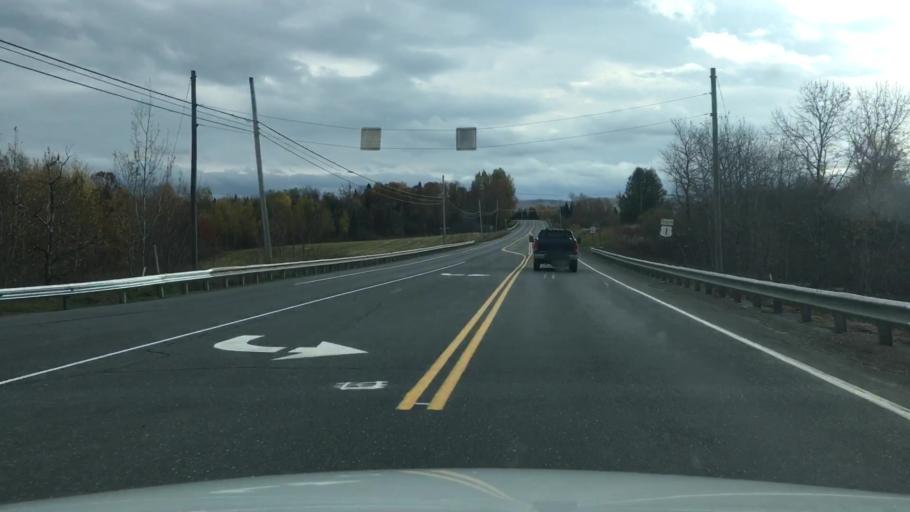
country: US
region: Maine
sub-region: Aroostook County
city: Easton
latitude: 46.5684
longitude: -67.9500
